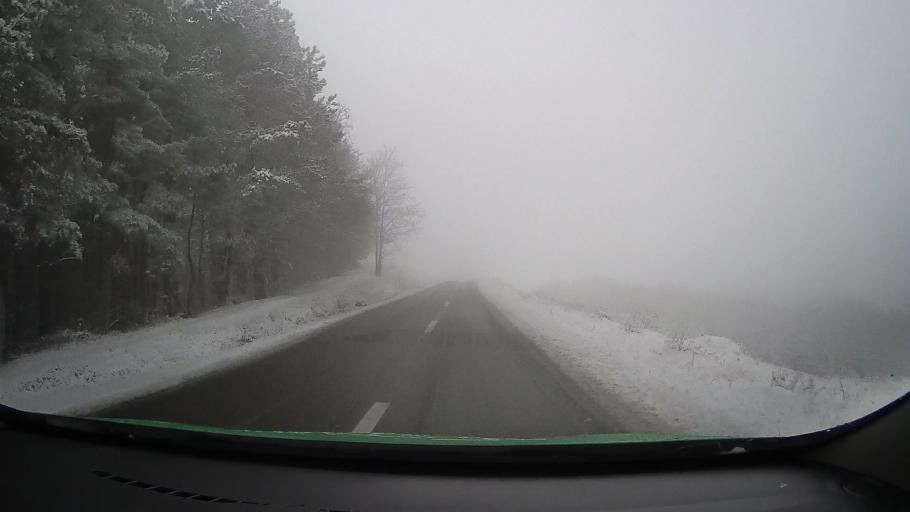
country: RO
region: Hunedoara
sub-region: Comuna Teliucu Inferior
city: Teliucu Inferior
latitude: 45.6692
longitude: 22.9178
